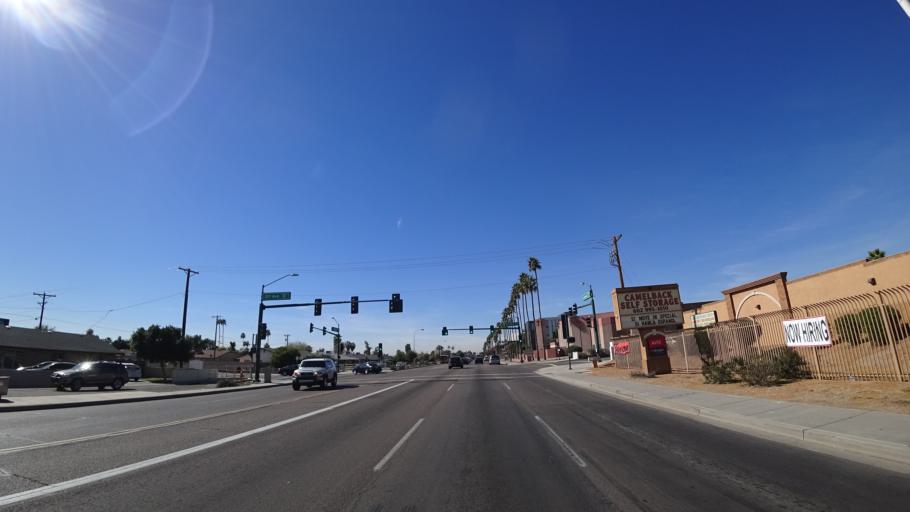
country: US
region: Arizona
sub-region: Maricopa County
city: Glendale
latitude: 33.5095
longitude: -112.1249
